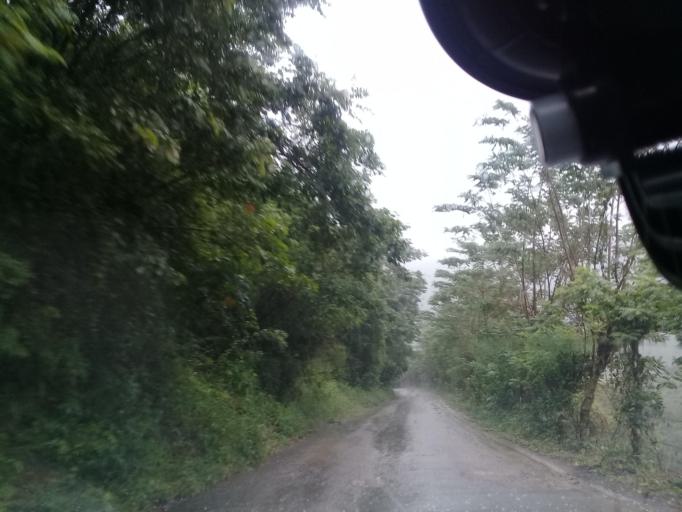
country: MX
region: Veracruz
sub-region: Chalma
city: San Pedro Coyutla
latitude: 21.2213
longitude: -98.4603
